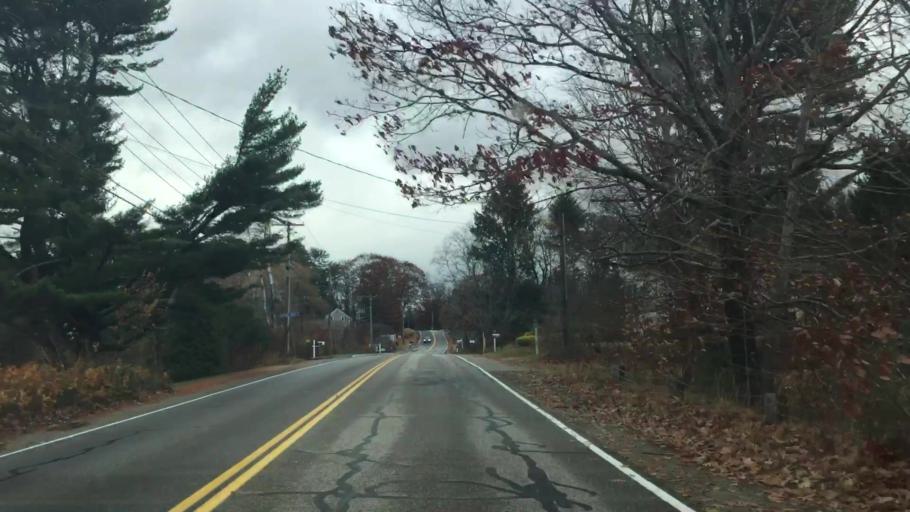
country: US
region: Maine
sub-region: York County
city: Kennebunkport
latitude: 43.3569
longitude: -70.4948
